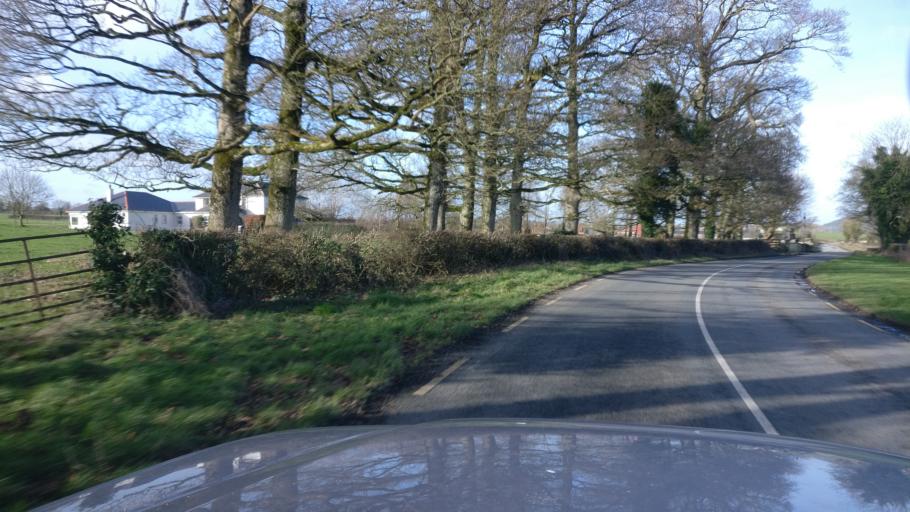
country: IE
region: Leinster
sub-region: Laois
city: Stradbally
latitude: 52.9770
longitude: -7.2149
